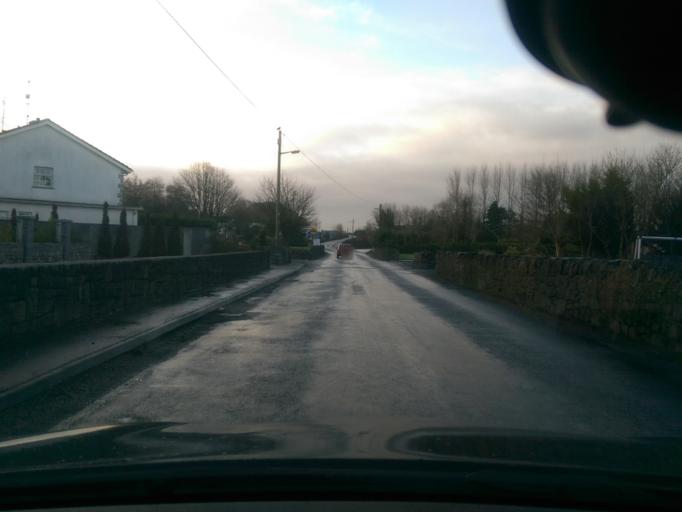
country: IE
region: Connaught
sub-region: County Galway
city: Athenry
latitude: 53.3080
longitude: -8.7405
